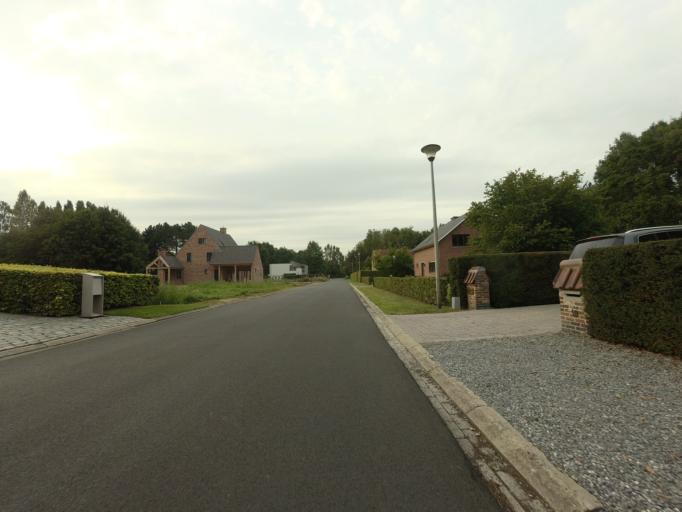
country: BE
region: Flanders
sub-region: Provincie Vlaams-Brabant
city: Kampenhout
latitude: 50.9439
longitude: 4.5610
